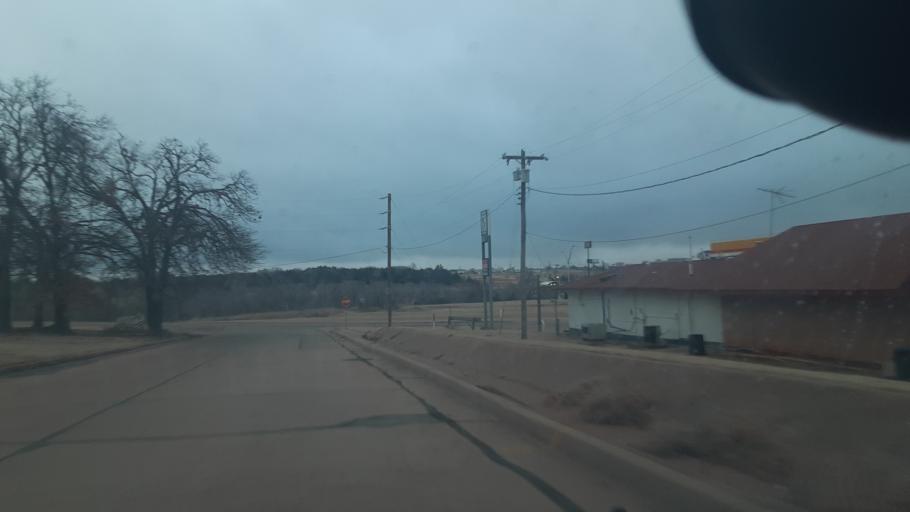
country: US
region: Oklahoma
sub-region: Logan County
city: Guthrie
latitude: 35.8773
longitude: -97.3987
